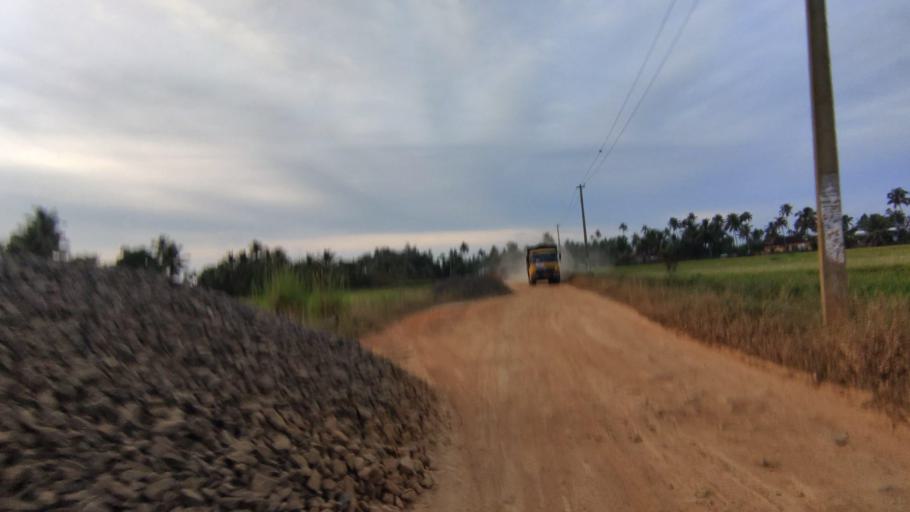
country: IN
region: Kerala
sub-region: Kottayam
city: Kottayam
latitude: 9.6462
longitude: 76.4804
